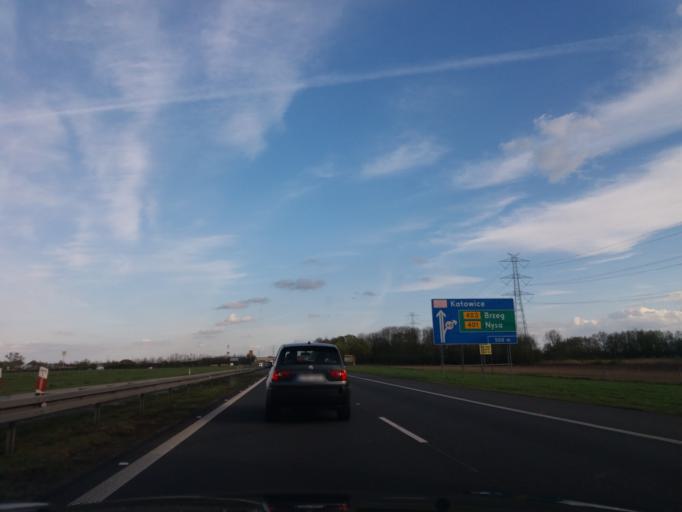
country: PL
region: Opole Voivodeship
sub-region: Powiat brzeski
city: Skarbimierz Osiedle
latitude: 50.7876
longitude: 17.3385
